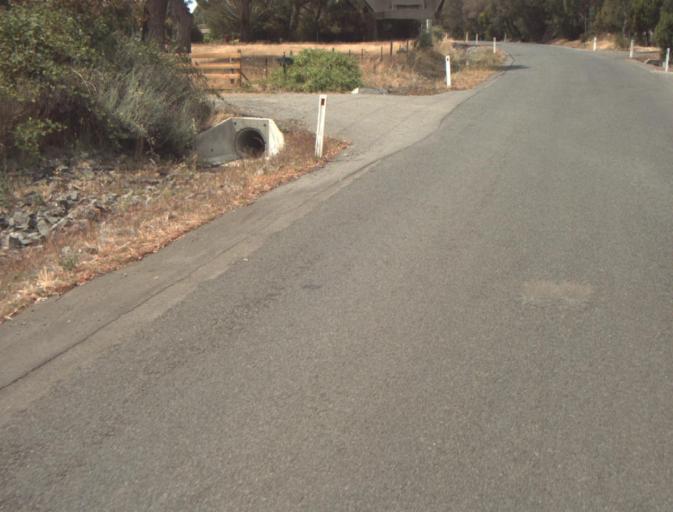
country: AU
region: Tasmania
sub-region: Launceston
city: Newstead
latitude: -41.4495
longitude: 147.2084
